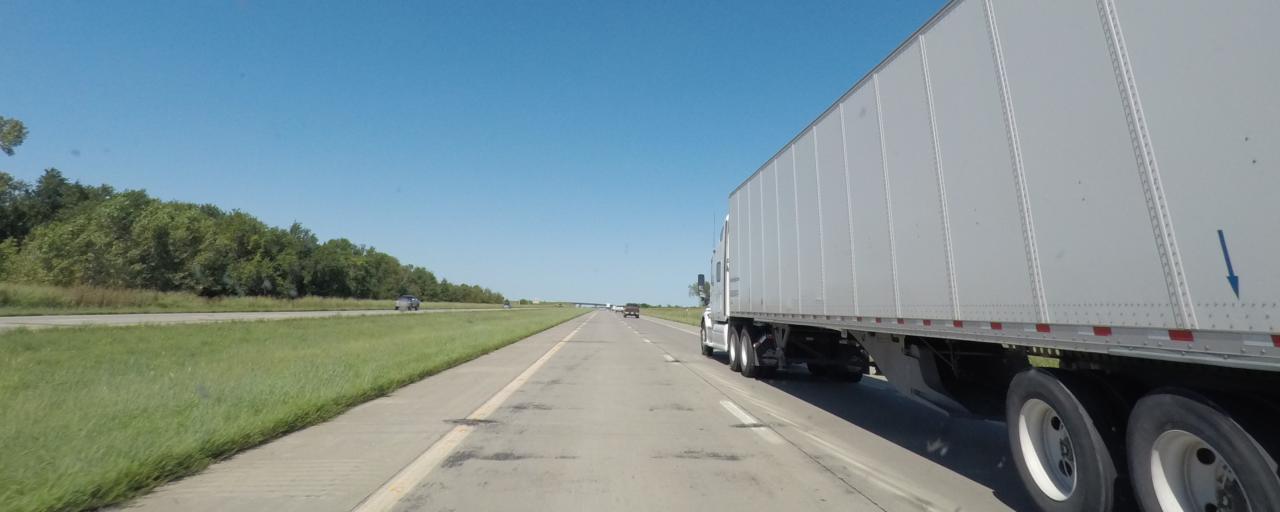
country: US
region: Kansas
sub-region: Franklin County
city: Ottawa
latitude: 38.6465
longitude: -95.2038
